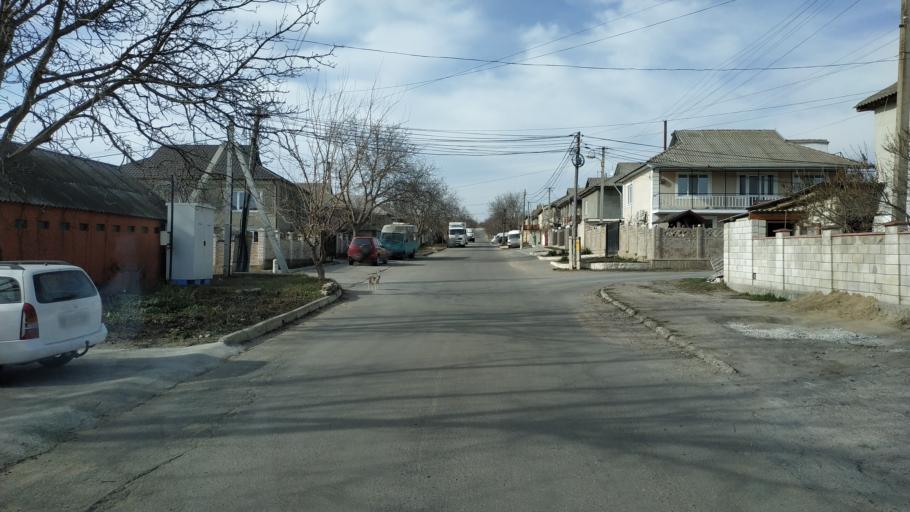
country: MD
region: Chisinau
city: Vatra
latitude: 47.0767
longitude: 28.6907
